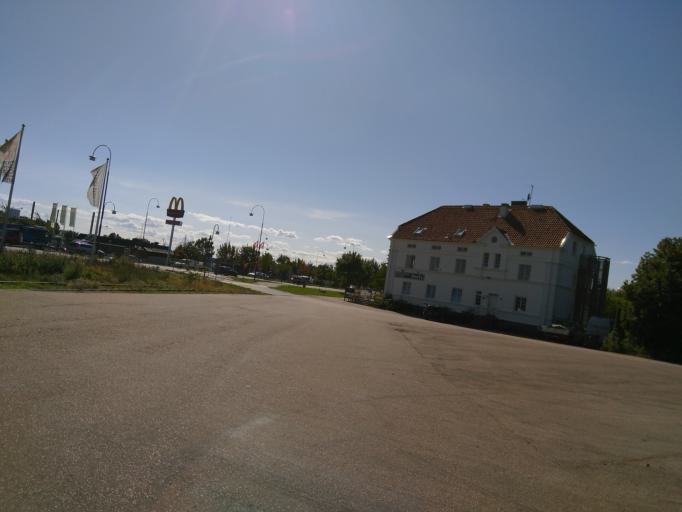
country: SE
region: Skane
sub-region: Landskrona
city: Landskrona
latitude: 55.8727
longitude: 12.8554
